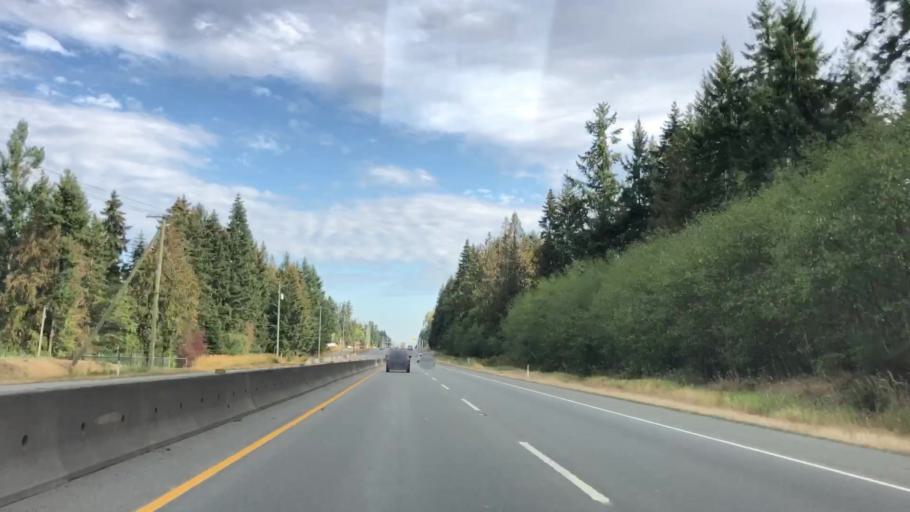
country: CA
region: British Columbia
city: Duncan
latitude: 48.7005
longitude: -123.5980
